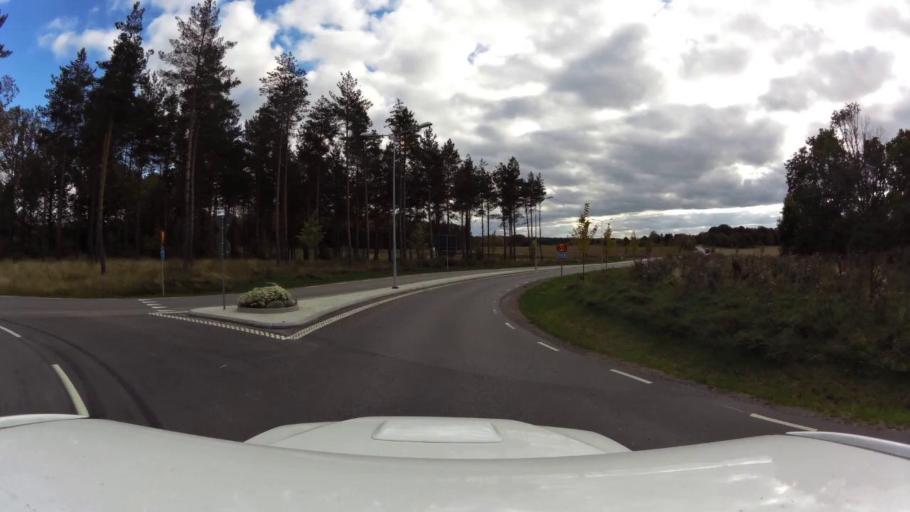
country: SE
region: OEstergoetland
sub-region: Linkopings Kommun
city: Linkoping
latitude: 58.3866
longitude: 15.5919
